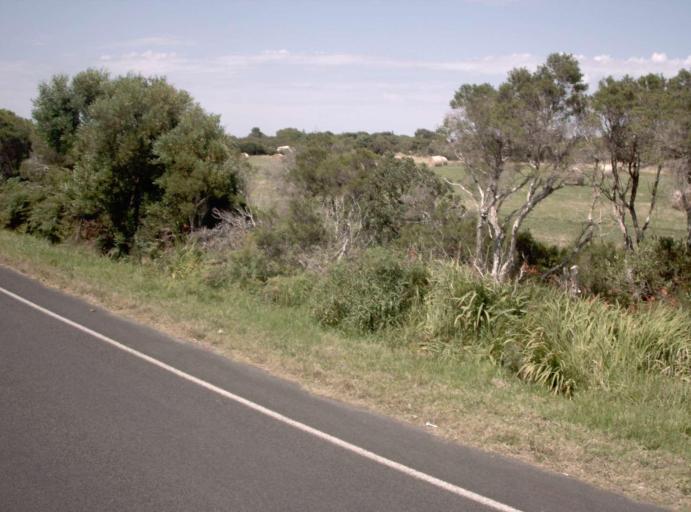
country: AU
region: Victoria
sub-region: Bass Coast
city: North Wonthaggi
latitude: -38.6629
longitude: 145.6194
